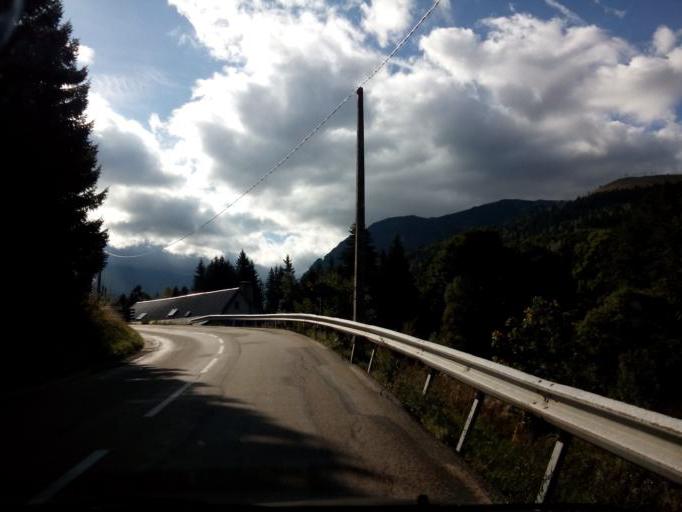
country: FR
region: Rhone-Alpes
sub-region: Departement de l'Isere
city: Vaulnaveys-le-Bas
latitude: 45.0359
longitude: 5.8502
